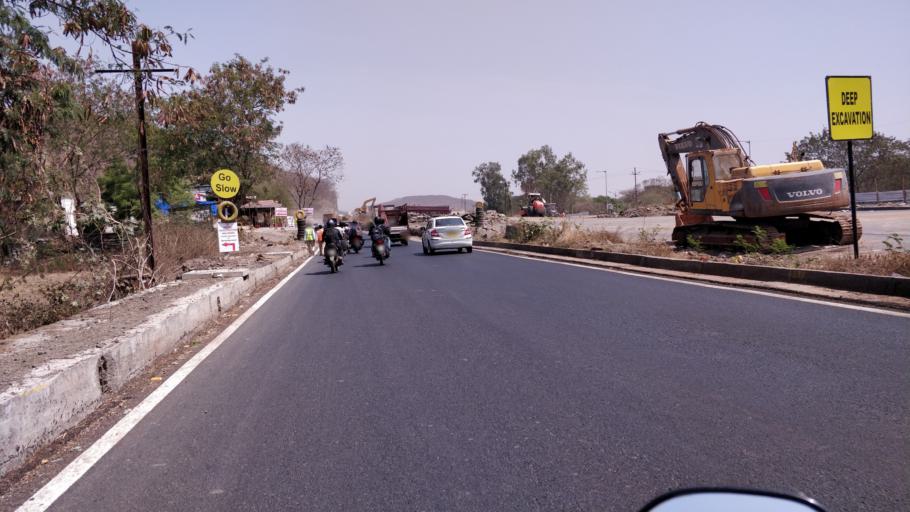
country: IN
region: Maharashtra
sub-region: Pune Division
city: Shivaji Nagar
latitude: 18.5327
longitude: 73.7797
